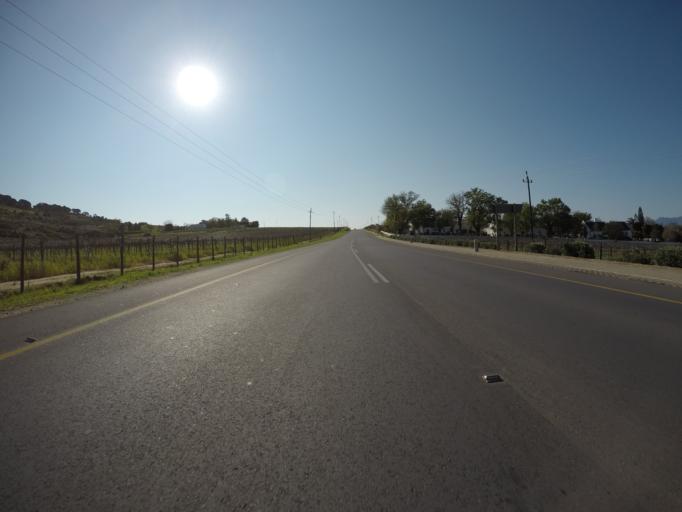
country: ZA
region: Western Cape
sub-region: Cape Winelands District Municipality
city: Noorder-Paarl
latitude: -33.6872
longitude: 18.9492
